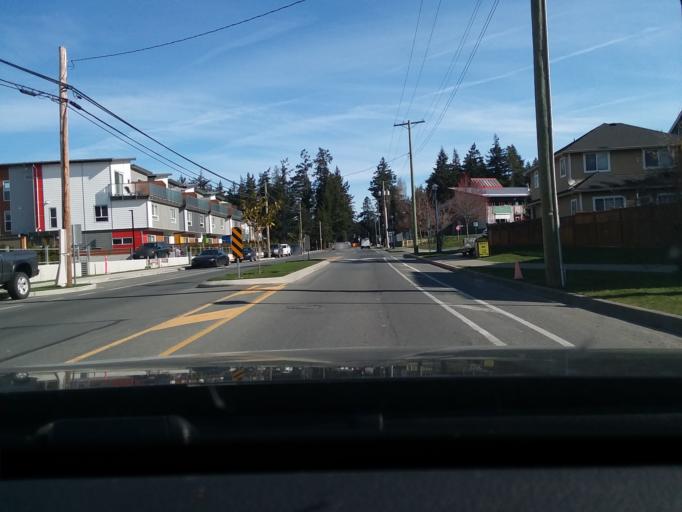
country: CA
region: British Columbia
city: Langford
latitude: 48.4273
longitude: -123.5304
